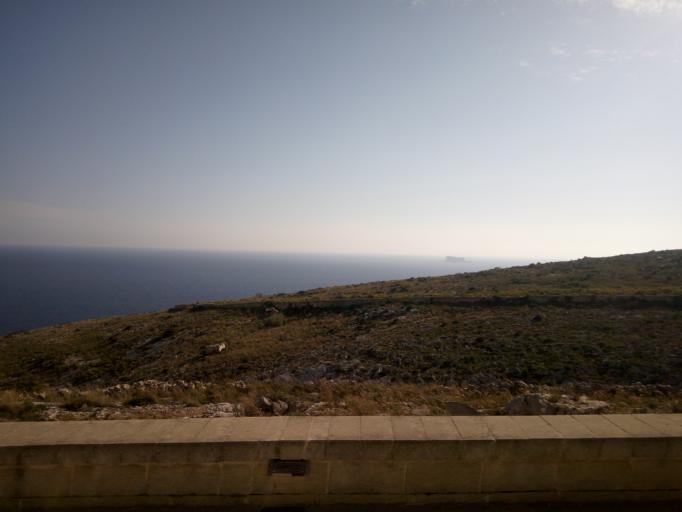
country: MT
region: Il-Qrendi
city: Qrendi
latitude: 35.8243
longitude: 14.4509
